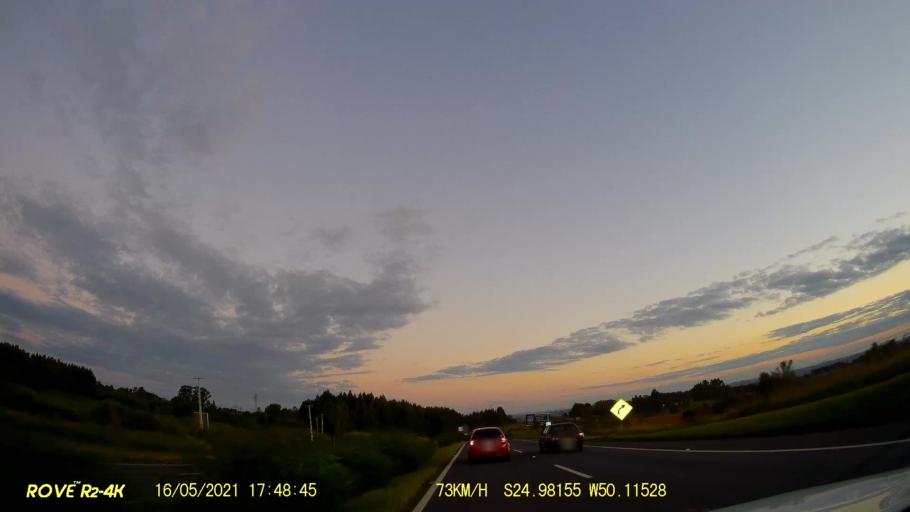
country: BR
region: Parana
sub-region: Carambei
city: Carambei
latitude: -24.9810
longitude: -50.1165
